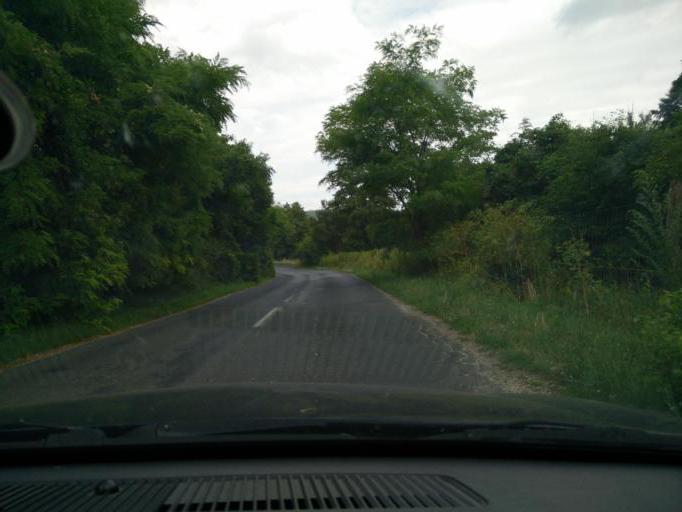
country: HU
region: Komarom-Esztergom
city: Baj
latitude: 47.6675
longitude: 18.3922
